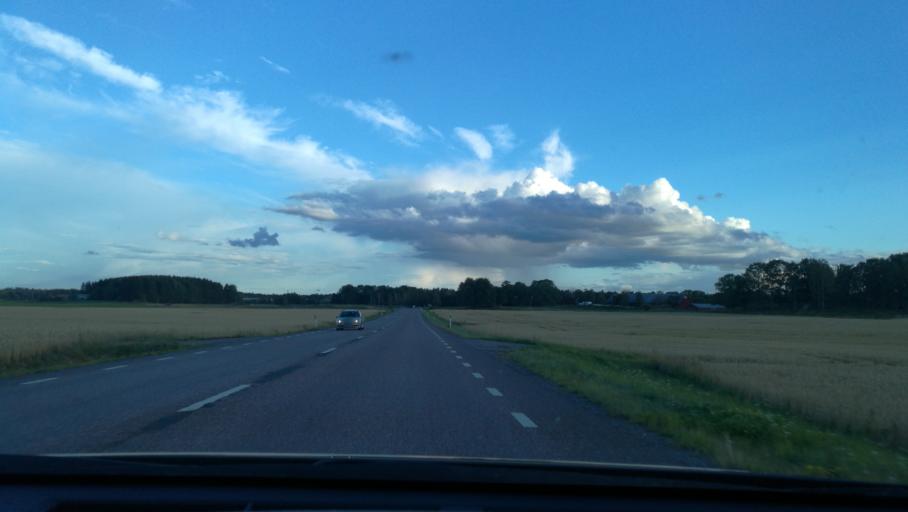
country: SE
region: Soedermanland
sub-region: Katrineholms Kommun
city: Katrineholm
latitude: 59.0237
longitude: 16.2139
